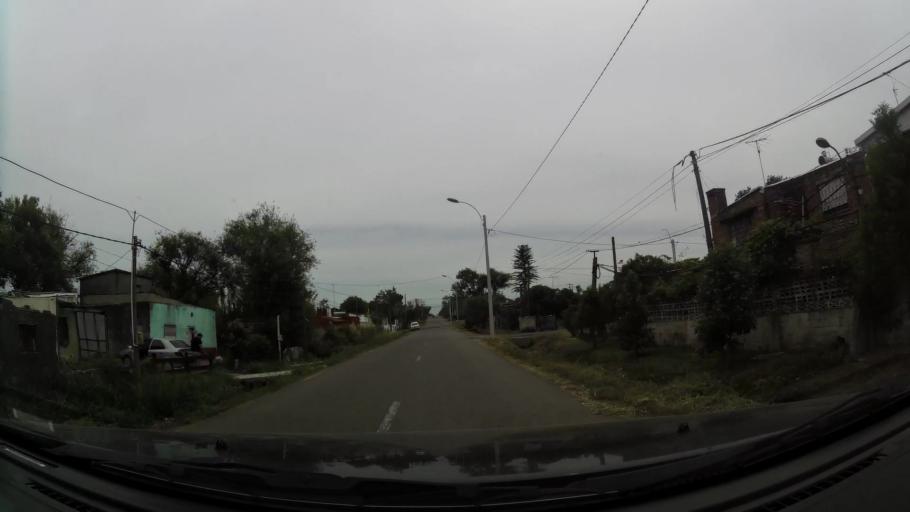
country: UY
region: Canelones
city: Las Piedras
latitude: -34.7402
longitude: -56.2313
